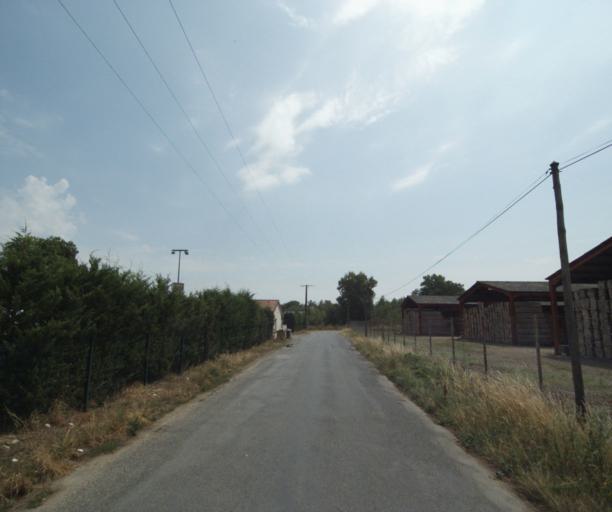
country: FR
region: Bourgogne
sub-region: Departement de Saone-et-Loire
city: Gueugnon
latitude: 46.5880
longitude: 4.0542
